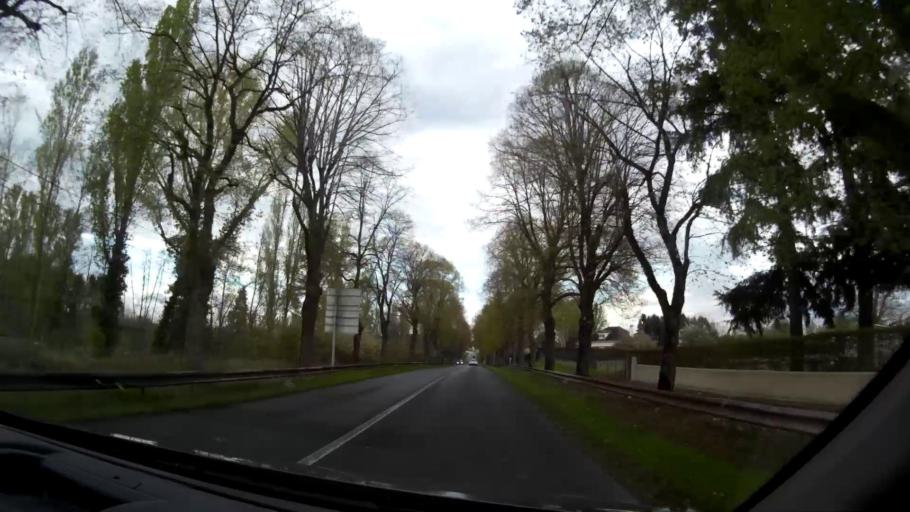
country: FR
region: Centre
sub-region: Departement du Loir-et-Cher
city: Contres
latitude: 47.4306
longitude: 1.4278
